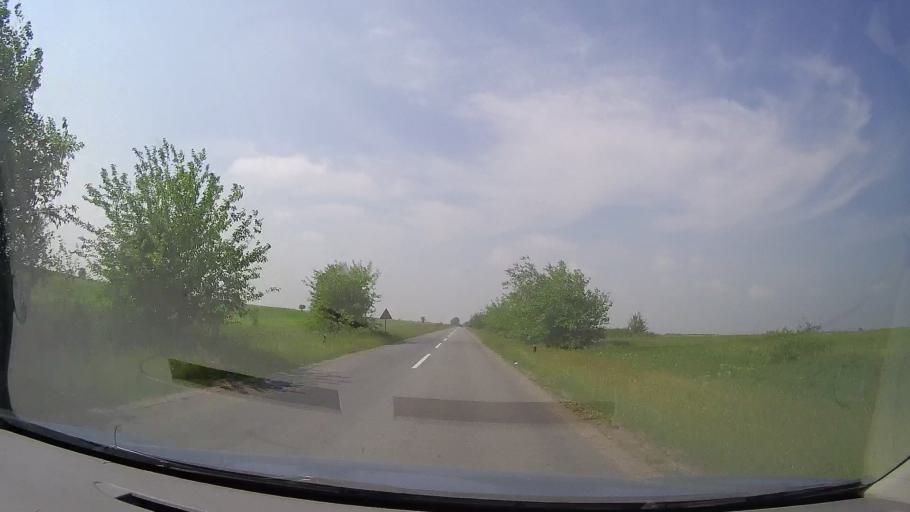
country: RS
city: Padina
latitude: 45.1503
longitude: 20.7446
